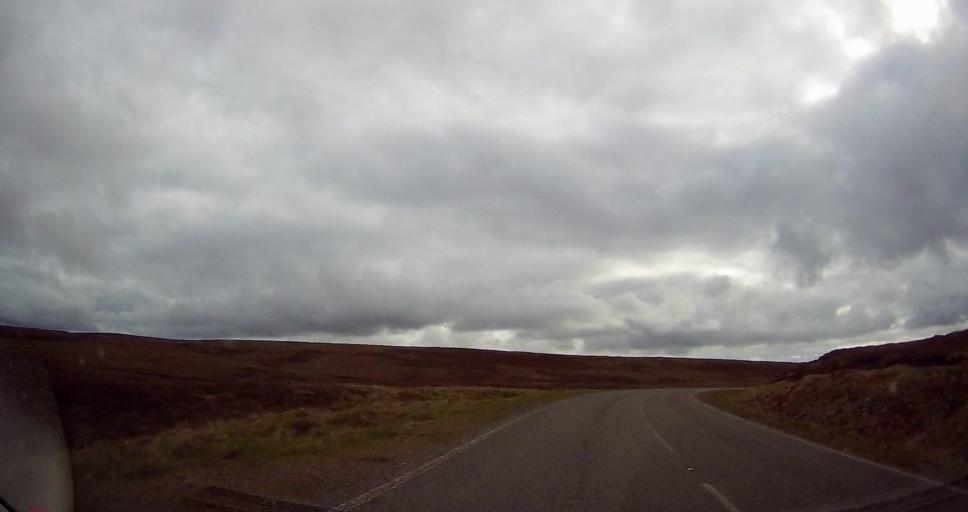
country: GB
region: Scotland
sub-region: Shetland Islands
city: Shetland
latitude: 60.6654
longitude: -1.0343
